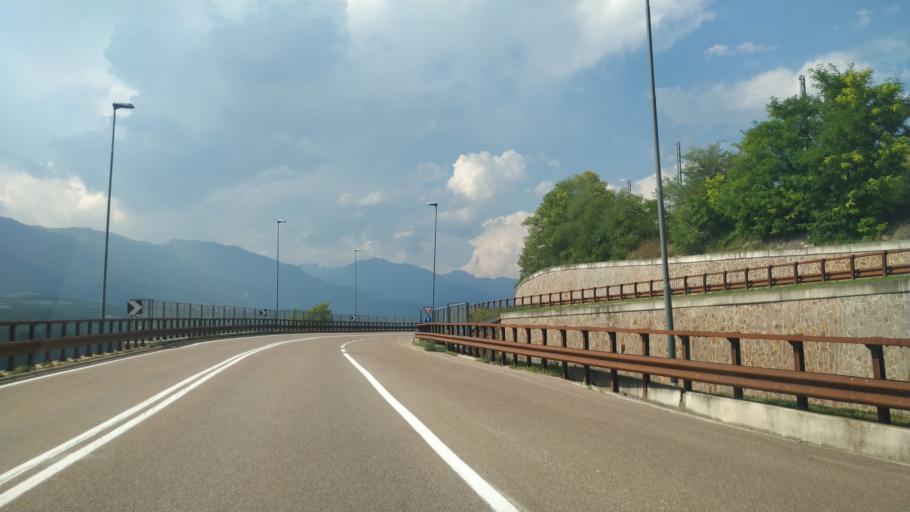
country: IT
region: Trentino-Alto Adige
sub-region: Provincia di Trento
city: Taio
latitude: 46.3070
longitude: 11.0697
